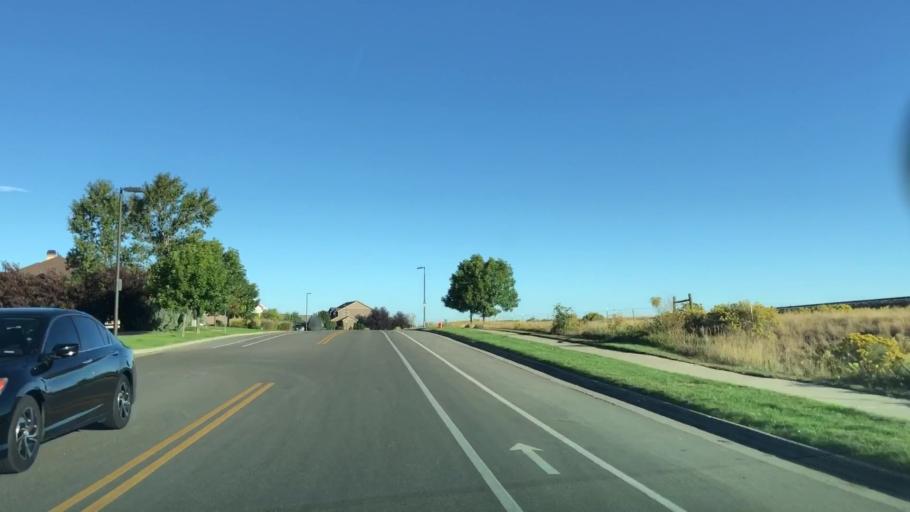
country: US
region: Colorado
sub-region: Larimer County
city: Loveland
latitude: 40.4513
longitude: -105.0257
